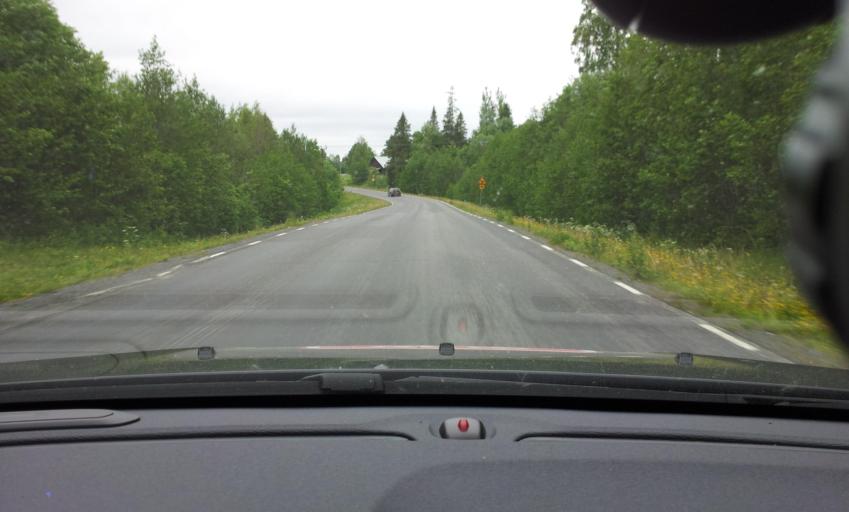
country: SE
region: Jaemtland
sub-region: Are Kommun
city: Jarpen
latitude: 63.3061
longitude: 13.6824
